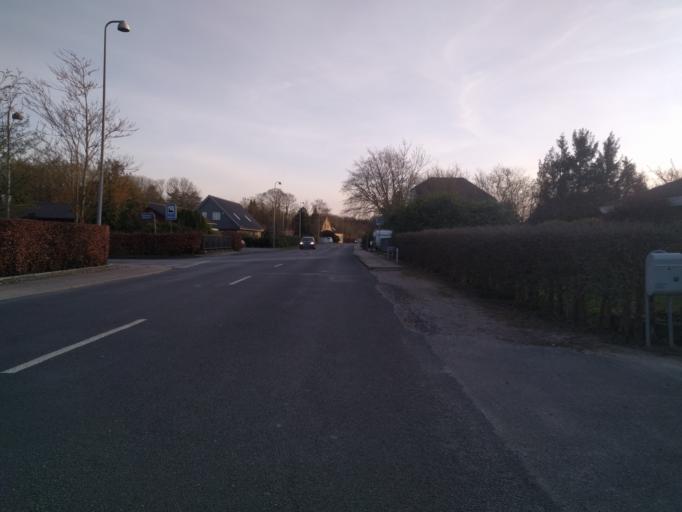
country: DK
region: South Denmark
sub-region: Odense Kommune
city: Bullerup
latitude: 55.4308
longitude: 10.4855
